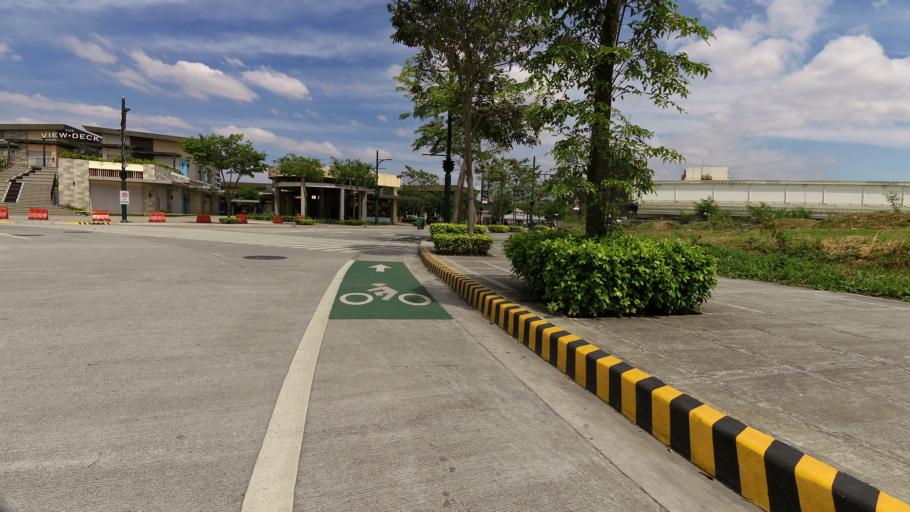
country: PH
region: Metro Manila
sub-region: Pasig
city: Pasig City
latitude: 14.5776
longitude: 121.0765
